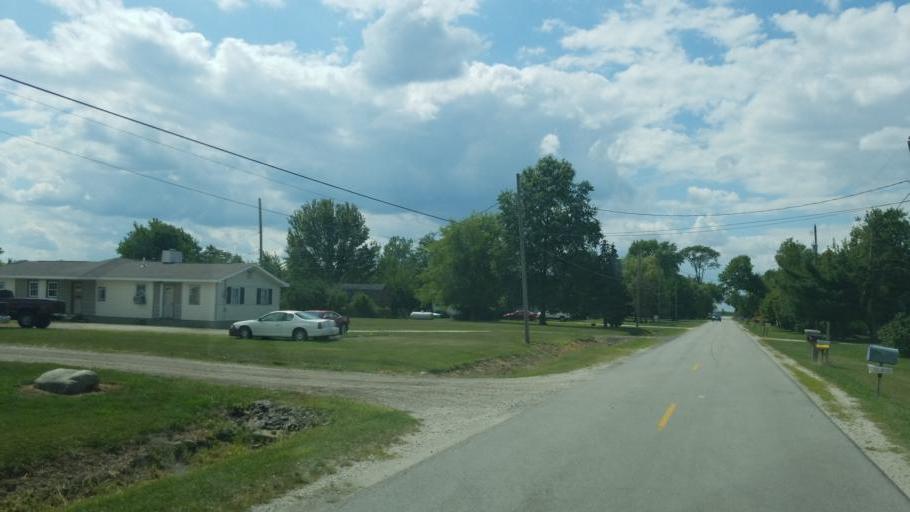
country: US
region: Ohio
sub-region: Lucas County
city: Curtice
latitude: 41.6555
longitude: -83.2680
